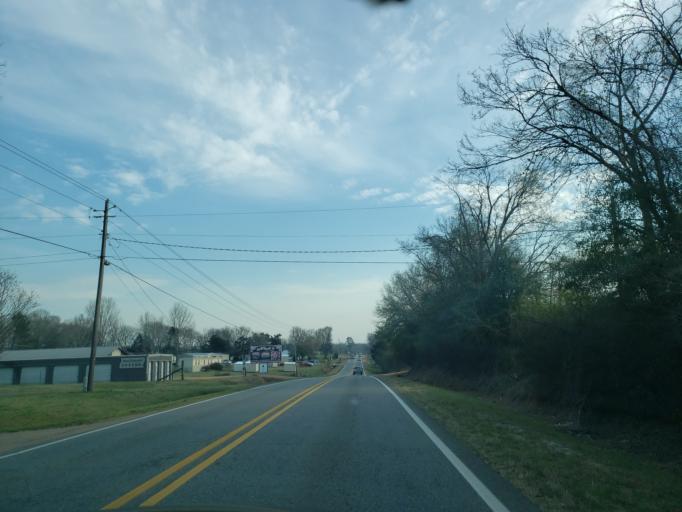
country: US
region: Alabama
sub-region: Hale County
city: Moundville
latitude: 32.9775
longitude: -87.6246
